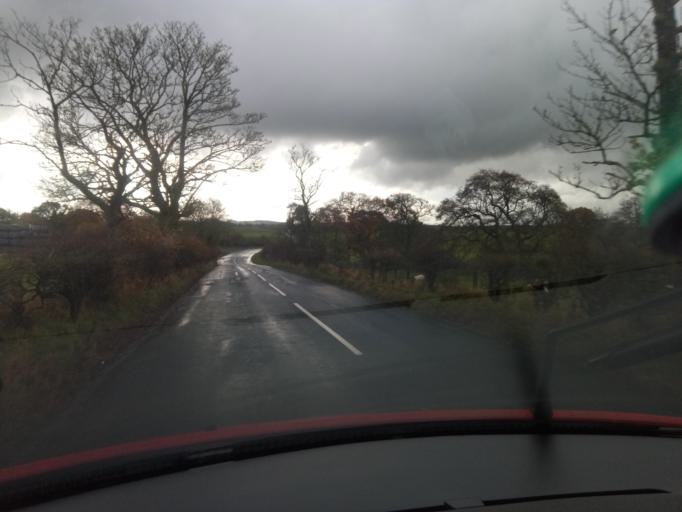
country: GB
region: England
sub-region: Northumberland
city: Birtley
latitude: 55.1160
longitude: -2.2407
